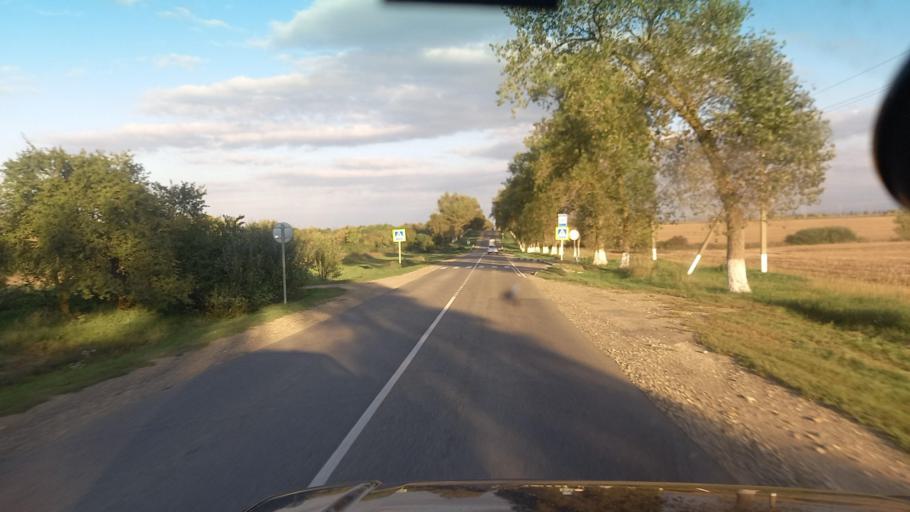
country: RU
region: Krasnodarskiy
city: Krymsk
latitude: 44.9402
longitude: 37.9269
